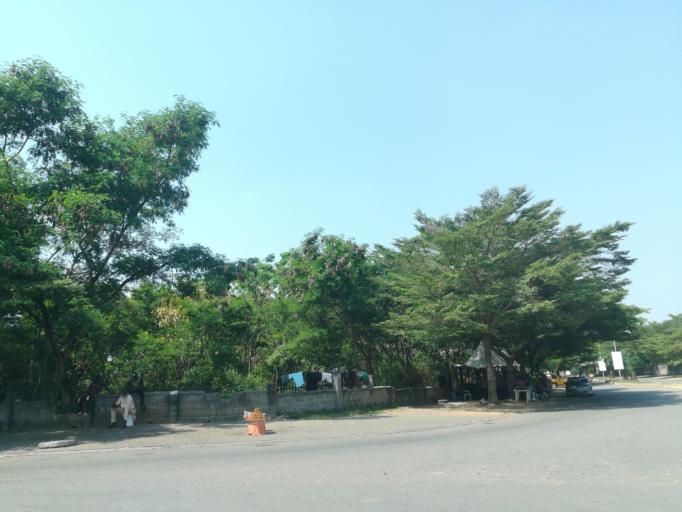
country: NG
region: Abuja Federal Capital Territory
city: Abuja
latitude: 9.0722
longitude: 7.4289
